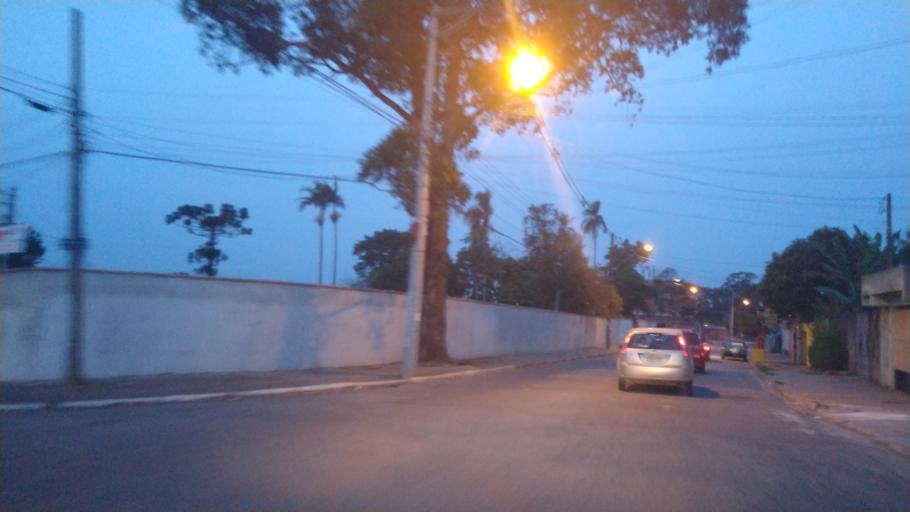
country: BR
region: Sao Paulo
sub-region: Aruja
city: Aruja
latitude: -23.4084
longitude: -46.4013
